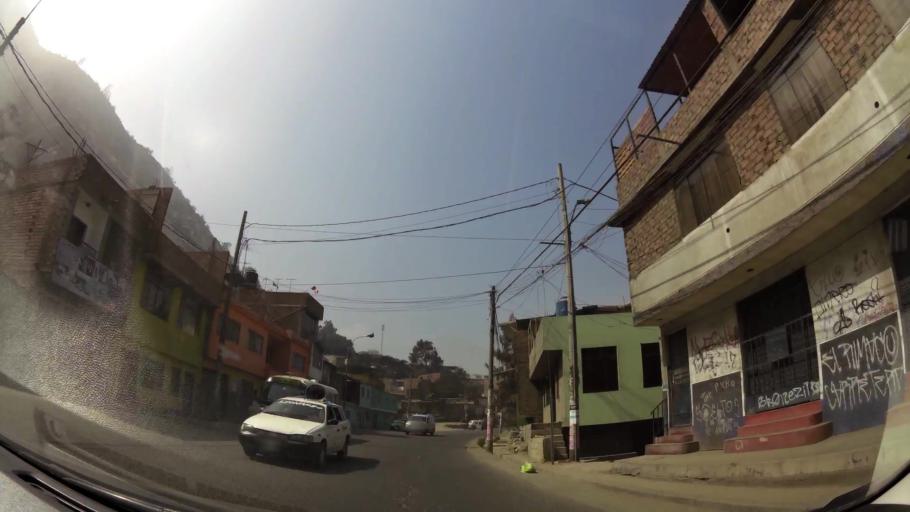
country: PE
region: Lima
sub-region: Lima
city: Asentamiento Humano Nicolas de Pierola
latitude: -11.9239
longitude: -76.6834
